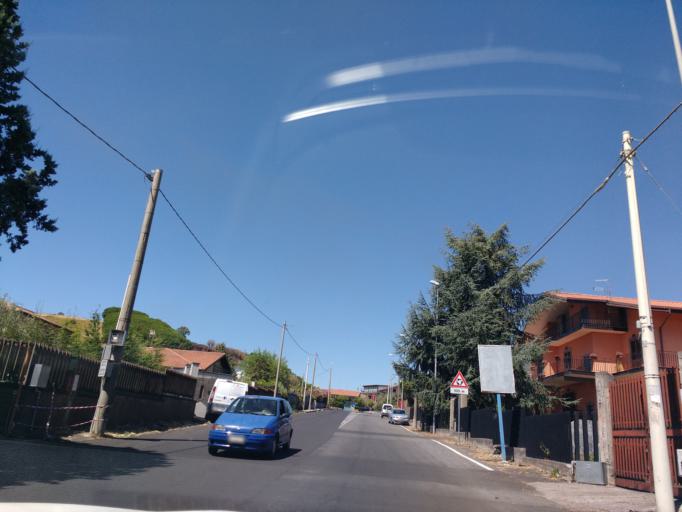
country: IT
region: Sicily
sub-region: Catania
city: Nicolosi
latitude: 37.6097
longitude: 15.0235
